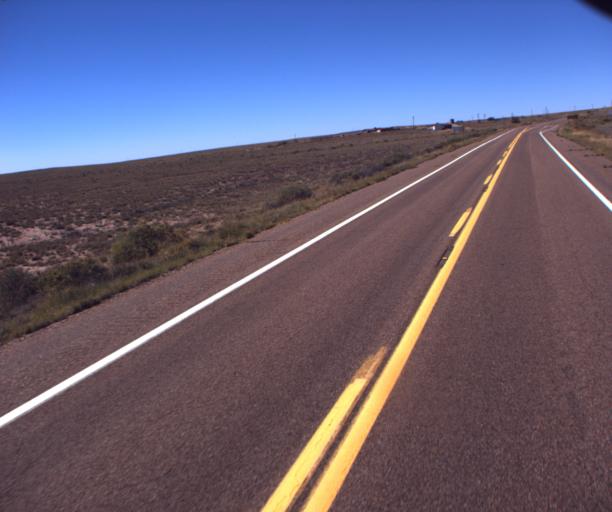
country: US
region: Arizona
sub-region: Navajo County
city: Holbrook
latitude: 34.7904
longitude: -109.8894
